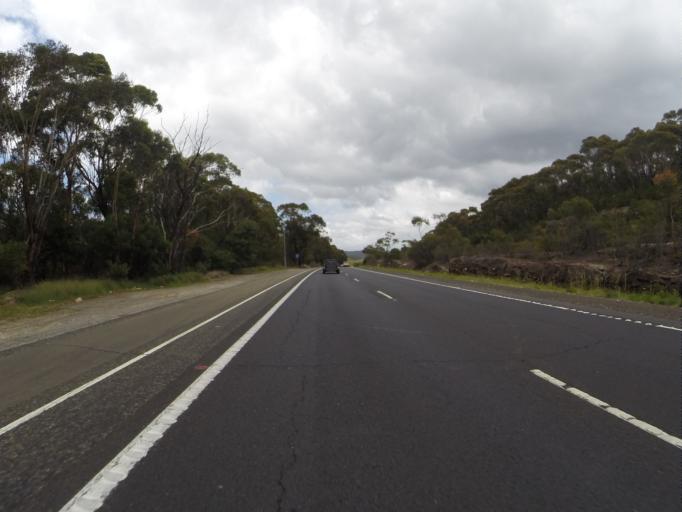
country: AU
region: New South Wales
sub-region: Wollongong
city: Helensburgh
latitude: -34.1761
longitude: 150.9770
